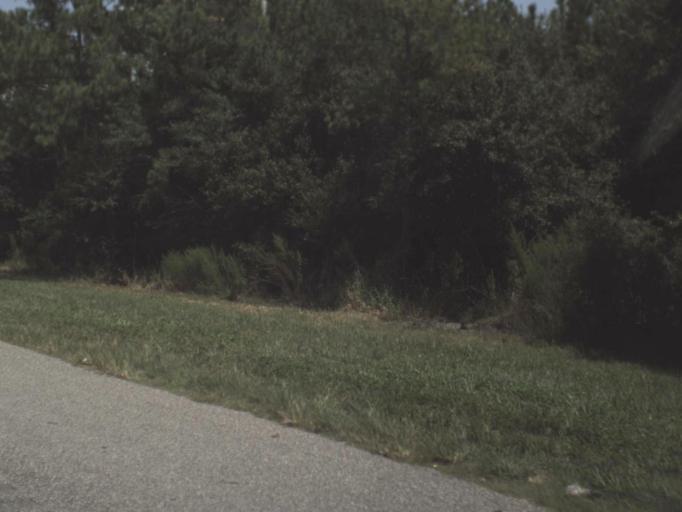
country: US
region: Florida
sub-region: Hillsborough County
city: Apollo Beach
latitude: 27.7973
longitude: -82.3547
